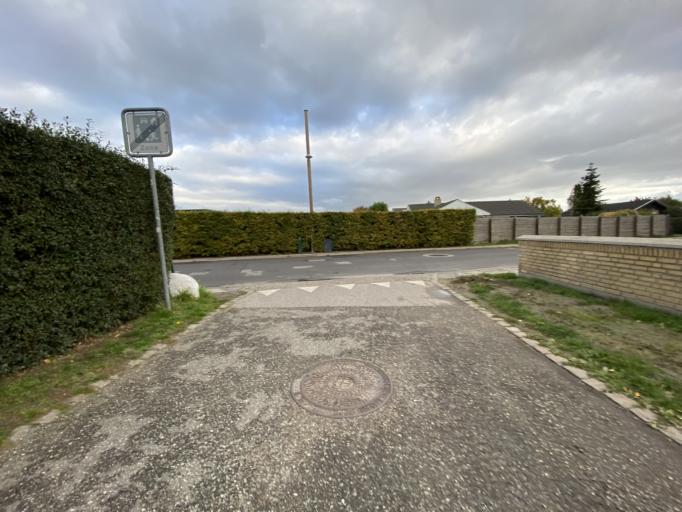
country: DK
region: Capital Region
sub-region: Dragor Kommune
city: Dragor
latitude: 55.5976
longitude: 12.6625
